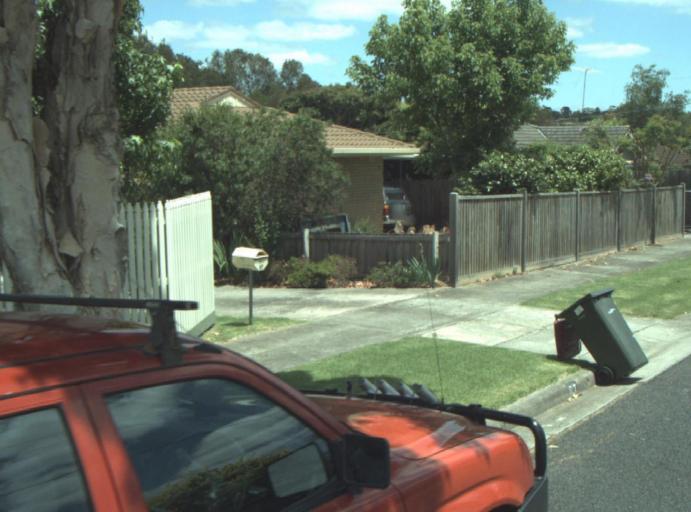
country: AU
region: Victoria
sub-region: Greater Geelong
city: Wandana Heights
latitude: -38.1804
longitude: 144.3256
